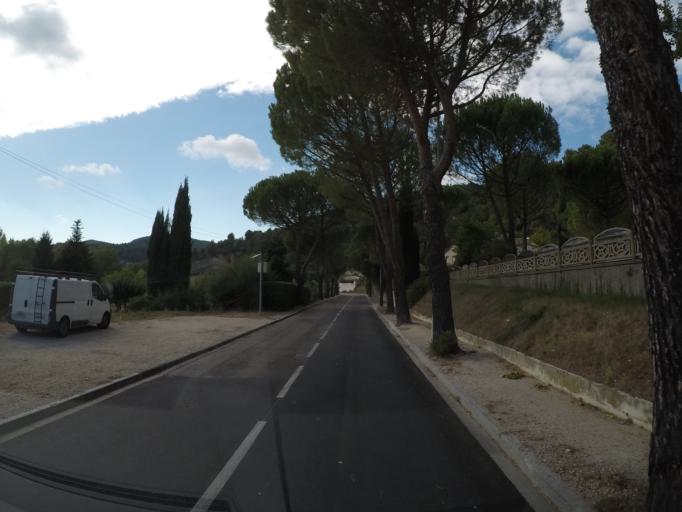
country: FR
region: Provence-Alpes-Cote d'Azur
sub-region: Departement du Vaucluse
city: Vaison-la-Romaine
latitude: 44.2408
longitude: 5.0644
